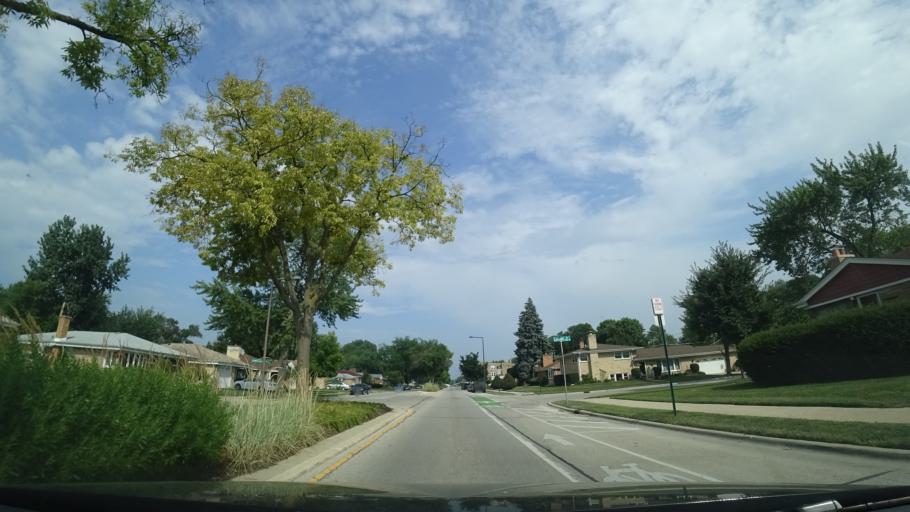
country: US
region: Illinois
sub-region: Cook County
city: Skokie
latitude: 42.0335
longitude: -87.7368
